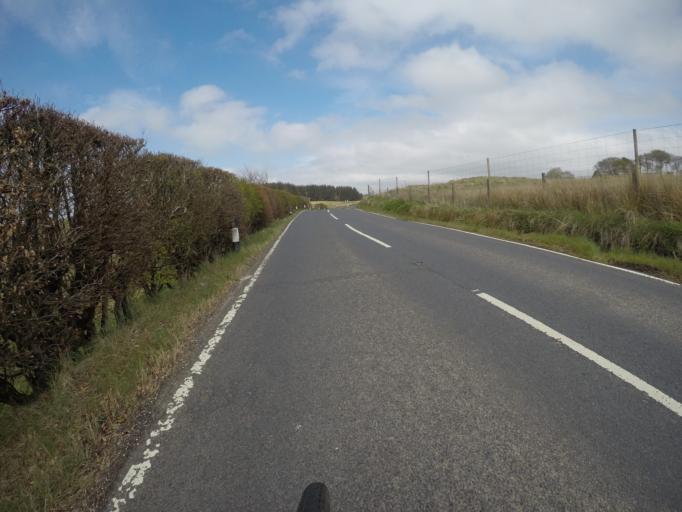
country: GB
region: Scotland
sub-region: East Renfrewshire
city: Neilston
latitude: 55.7216
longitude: -4.4308
